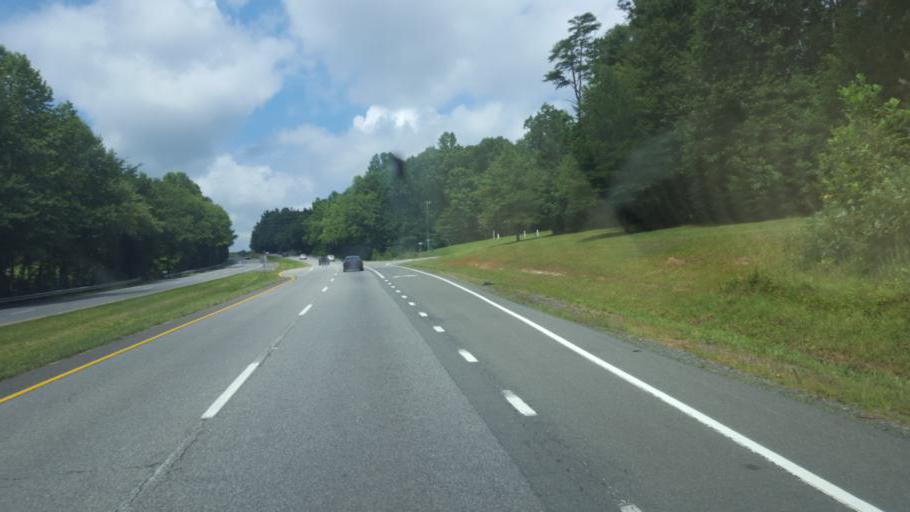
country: US
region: Virginia
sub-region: Stafford County
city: Falmouth
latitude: 38.4143
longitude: -77.6066
